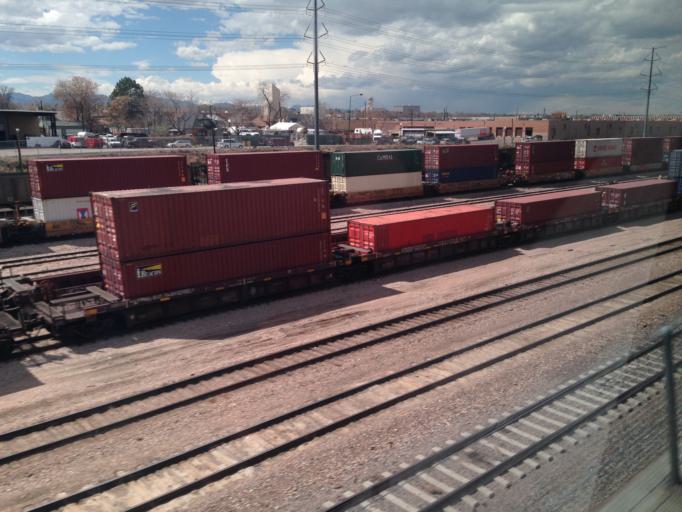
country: US
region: Colorado
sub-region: Adams County
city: Berkley
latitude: 39.7775
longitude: -104.9971
